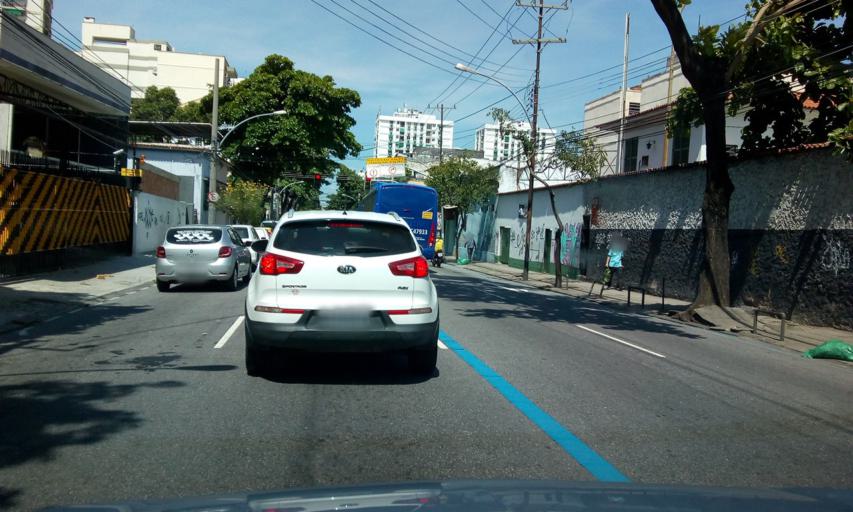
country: BR
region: Rio de Janeiro
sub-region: Rio De Janeiro
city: Rio de Janeiro
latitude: -22.9197
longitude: -43.2568
